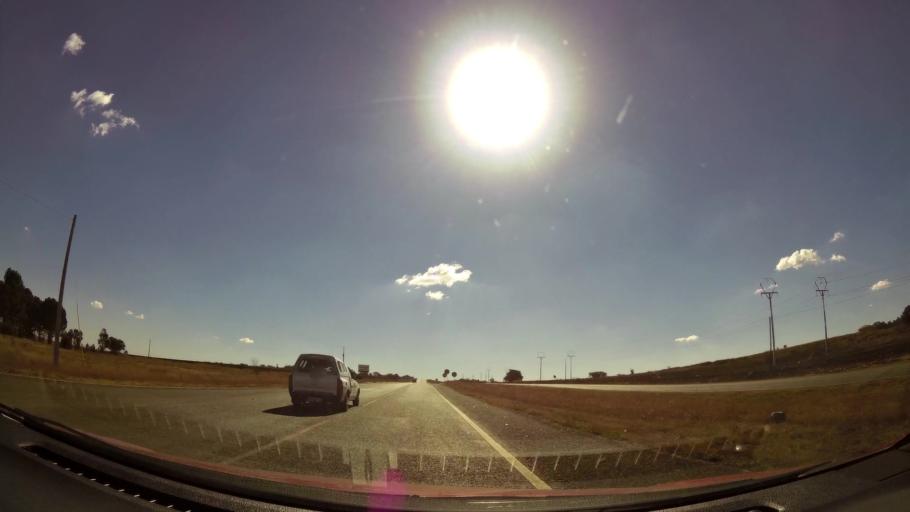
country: ZA
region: Gauteng
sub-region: West Rand District Municipality
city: Carletonville
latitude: -26.3925
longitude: 27.4182
